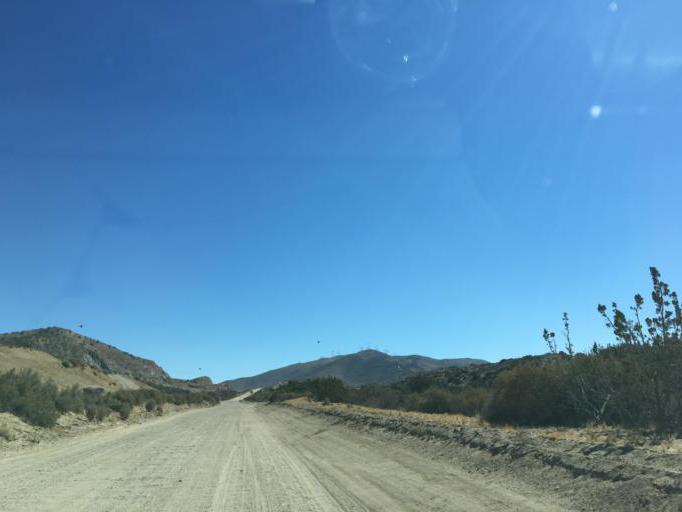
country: US
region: California
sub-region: Los Angeles County
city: Vincent
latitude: 34.4850
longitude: -118.1371
